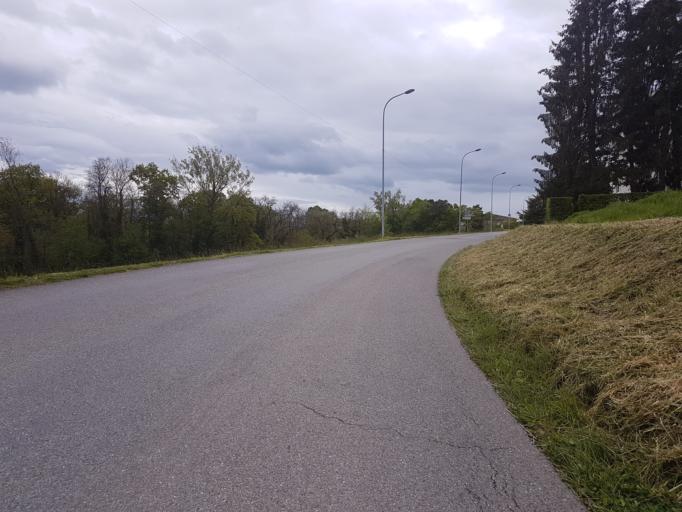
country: CH
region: Vaud
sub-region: Morges District
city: Preverenges
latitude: 46.5158
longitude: 6.5426
